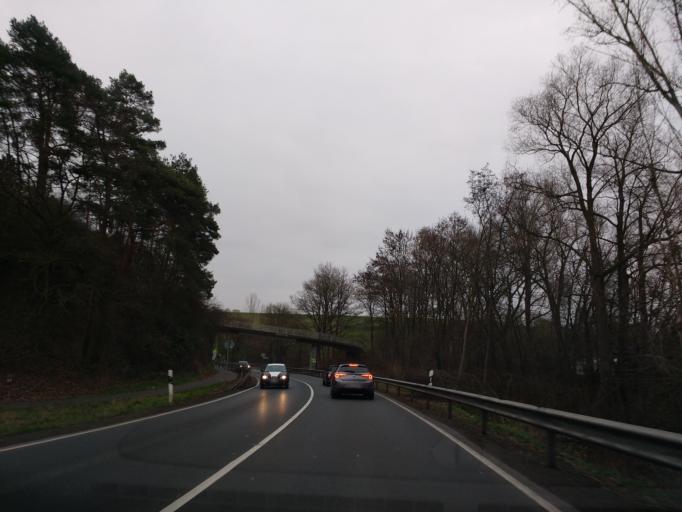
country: DE
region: Hesse
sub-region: Regierungsbezirk Kassel
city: Baunatal
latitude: 51.2127
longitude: 9.4352
